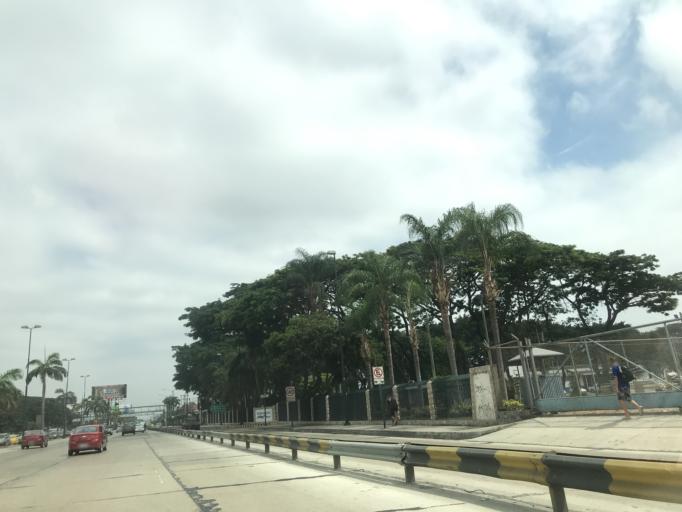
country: EC
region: Guayas
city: Eloy Alfaro
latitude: -2.1686
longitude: -79.8797
